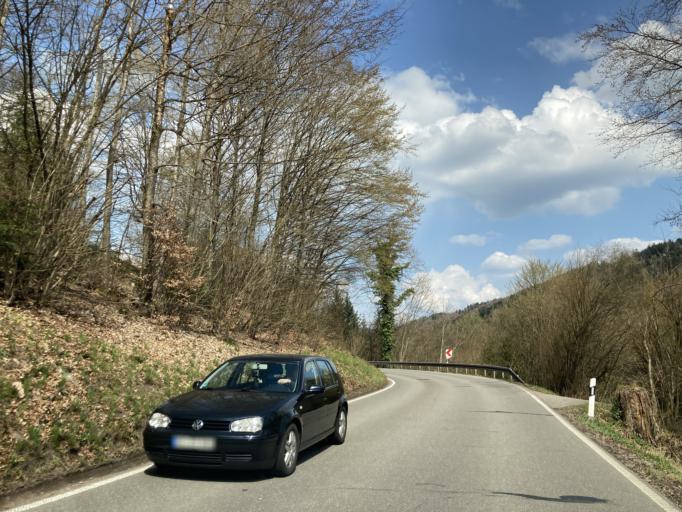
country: DE
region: Baden-Wuerttemberg
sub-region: Karlsruhe Region
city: Hofen an der Enz
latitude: 48.8250
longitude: 8.5730
